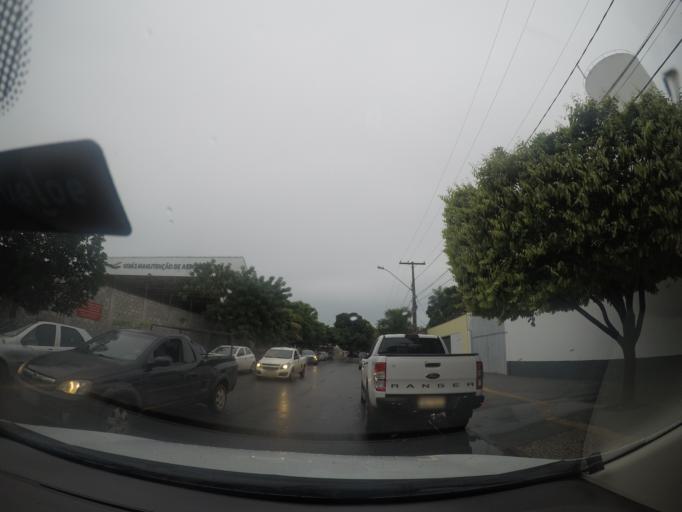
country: BR
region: Goias
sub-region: Goiania
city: Goiania
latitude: -16.6306
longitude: -49.2309
